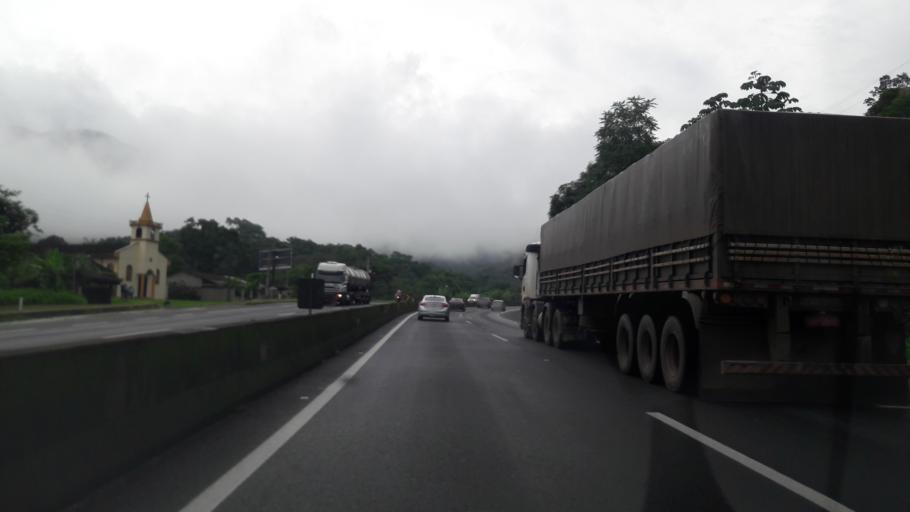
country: BR
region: Parana
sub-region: Antonina
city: Antonina
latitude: -25.5717
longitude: -48.8187
